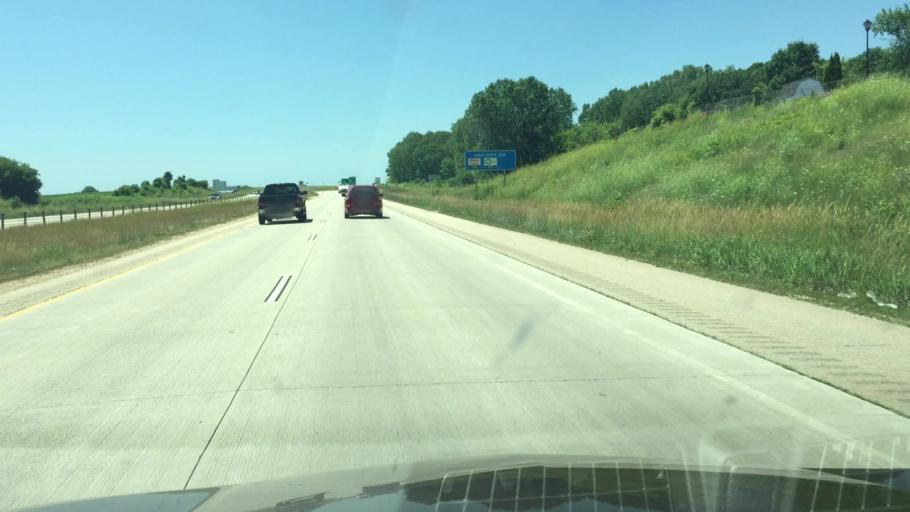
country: US
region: Wisconsin
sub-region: Dodge County
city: Beaver Dam
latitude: 43.4360
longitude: -88.8538
